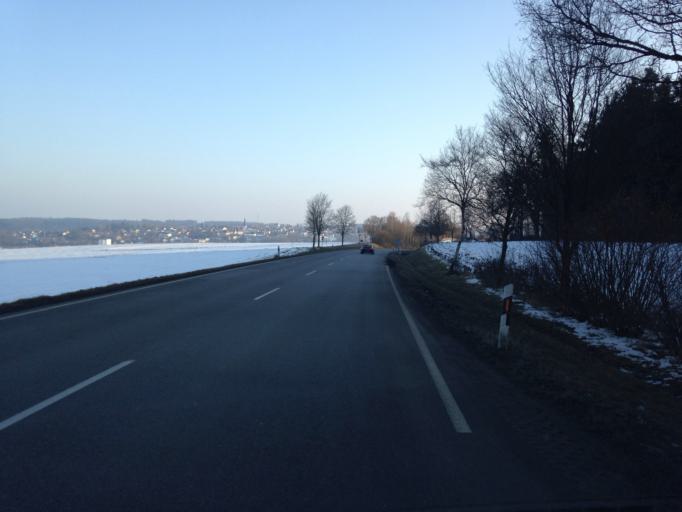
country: DE
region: Bavaria
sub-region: Lower Bavaria
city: Simbach
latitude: 48.5758
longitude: 12.7258
